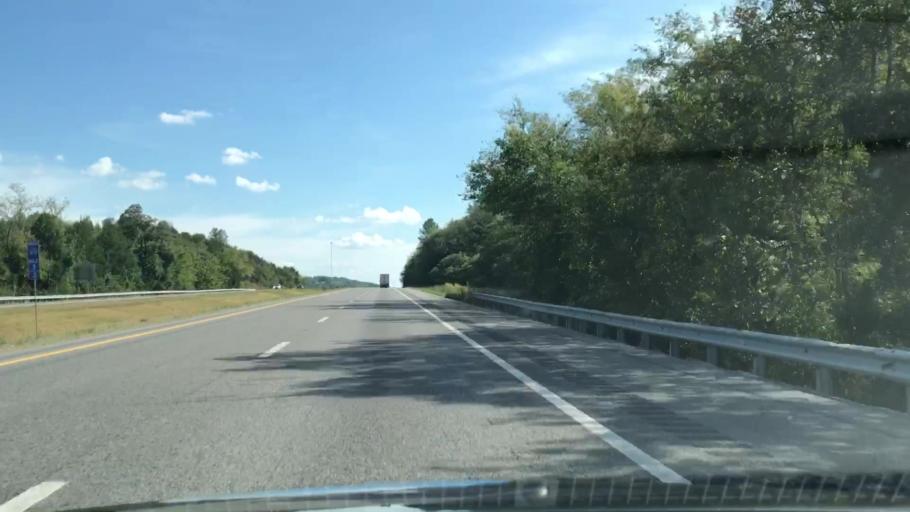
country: US
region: Alabama
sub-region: Limestone County
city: Ardmore
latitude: 35.0457
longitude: -86.8802
